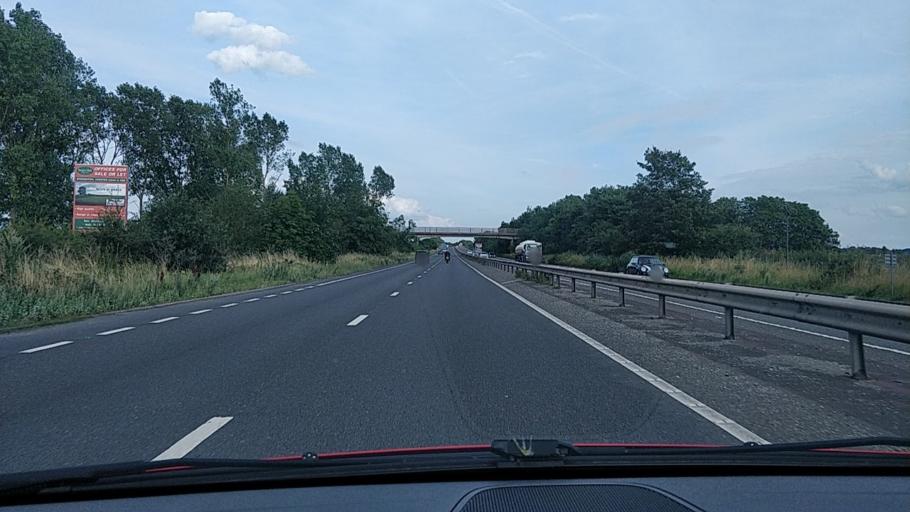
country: GB
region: Wales
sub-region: Wrexham
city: Rossett
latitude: 53.1591
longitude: -2.9447
